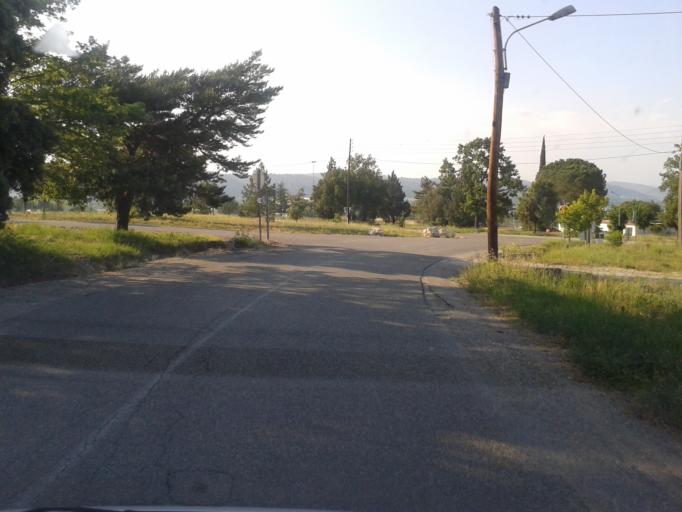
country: FR
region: Provence-Alpes-Cote d'Azur
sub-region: Departement du Vaucluse
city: Beaumont-de-Pertuis
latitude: 43.6951
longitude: 5.7365
